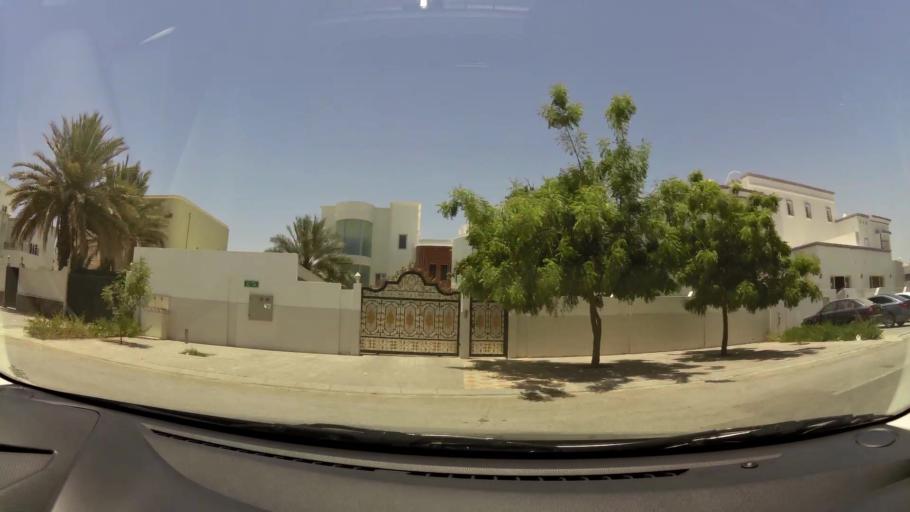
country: OM
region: Muhafazat Masqat
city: As Sib al Jadidah
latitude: 23.6336
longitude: 58.2363
